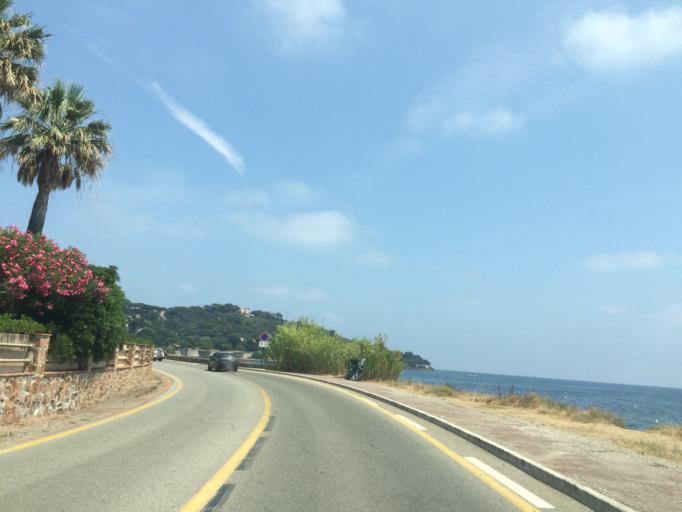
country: FR
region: Provence-Alpes-Cote d'Azur
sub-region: Departement du Var
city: Sainte-Maxime
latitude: 43.3112
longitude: 6.6537
